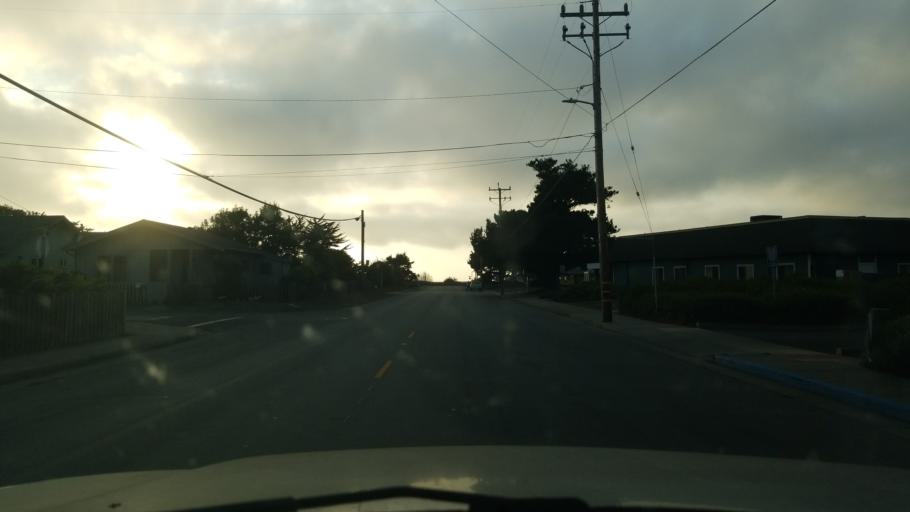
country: US
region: California
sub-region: Mendocino County
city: Fort Bragg
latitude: 39.4301
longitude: -123.8034
